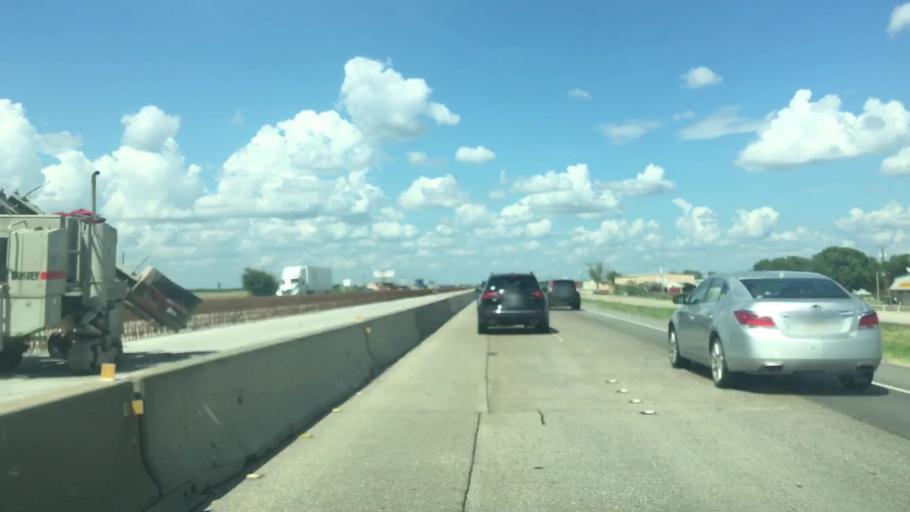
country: US
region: Texas
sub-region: Ellis County
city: Oak Leaf
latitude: 32.4773
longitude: -96.8347
